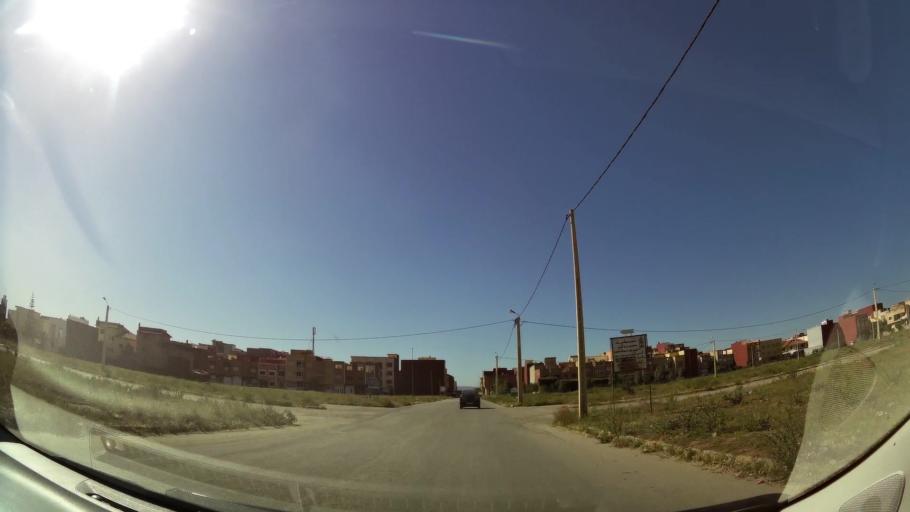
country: MA
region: Oriental
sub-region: Berkane-Taourirt
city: Berkane
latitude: 34.9422
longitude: -2.3362
